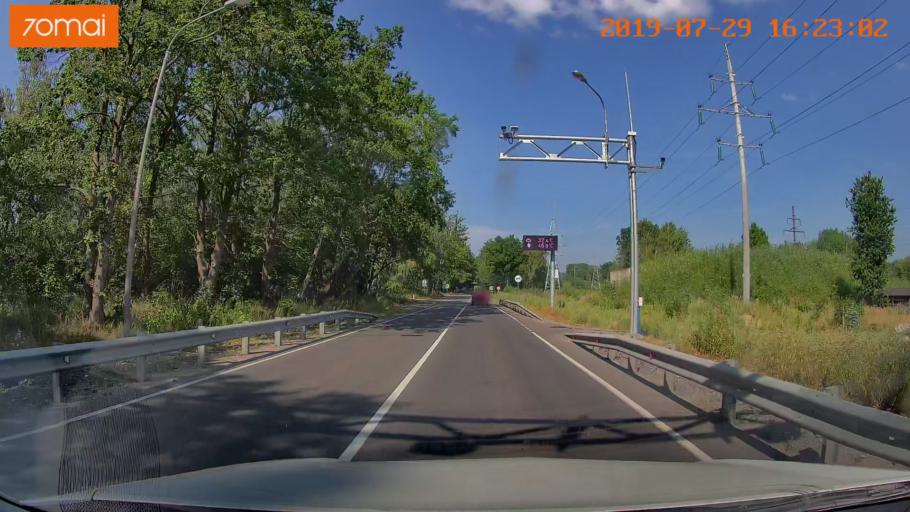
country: RU
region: Kaliningrad
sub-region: Gorod Kaliningrad
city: Baltiysk
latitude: 54.7029
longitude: 19.9435
